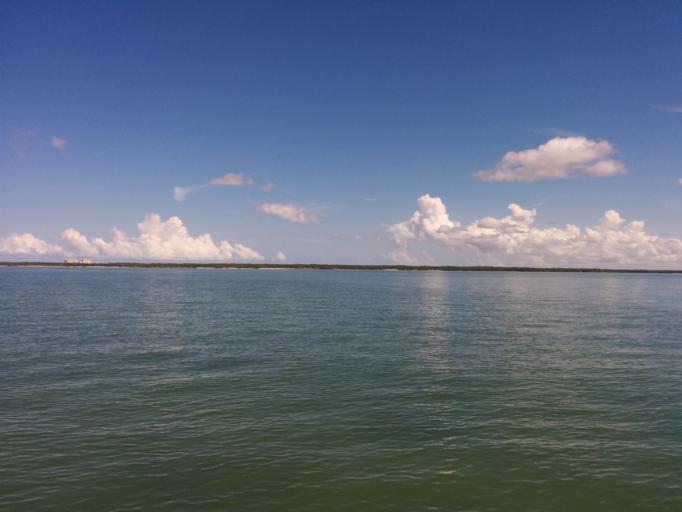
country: US
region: Florida
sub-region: Collier County
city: Marco
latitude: 25.8757
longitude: -81.6536
